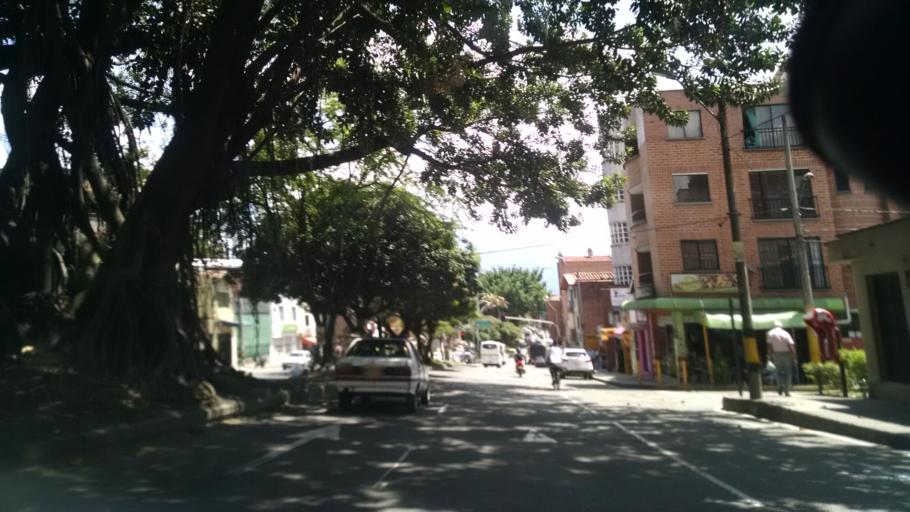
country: CO
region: Antioquia
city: Medellin
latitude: 6.2528
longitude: -75.6083
